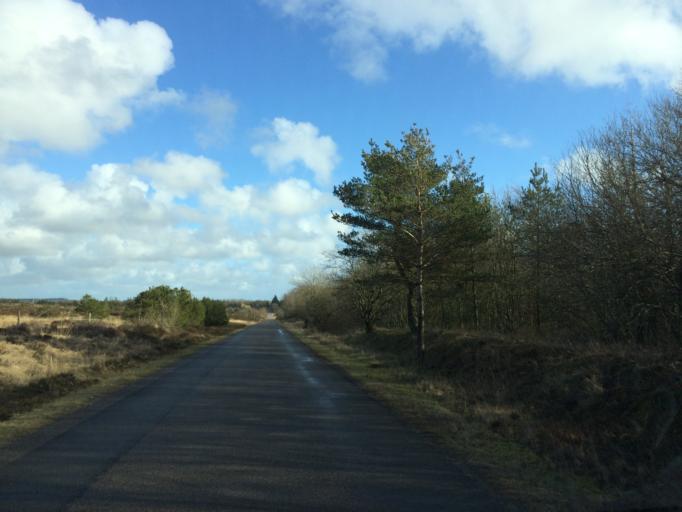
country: DK
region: Central Jutland
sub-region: Holstebro Kommune
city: Ulfborg
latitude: 56.2402
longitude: 8.4029
